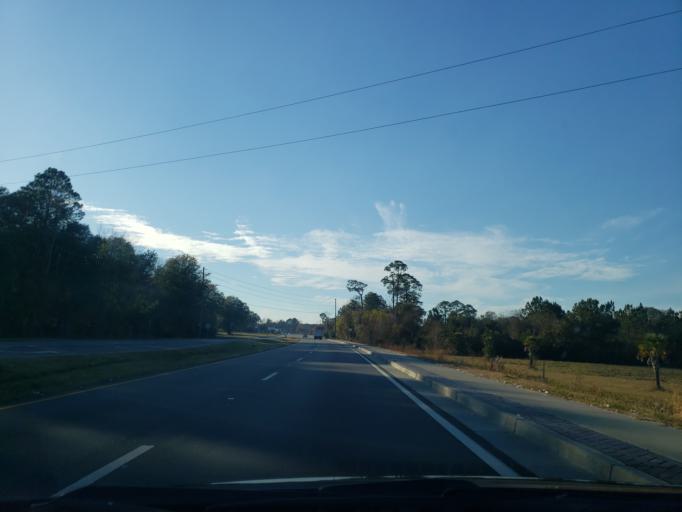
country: US
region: Georgia
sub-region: Atkinson County
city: Pearson
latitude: 31.2965
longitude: -82.8441
